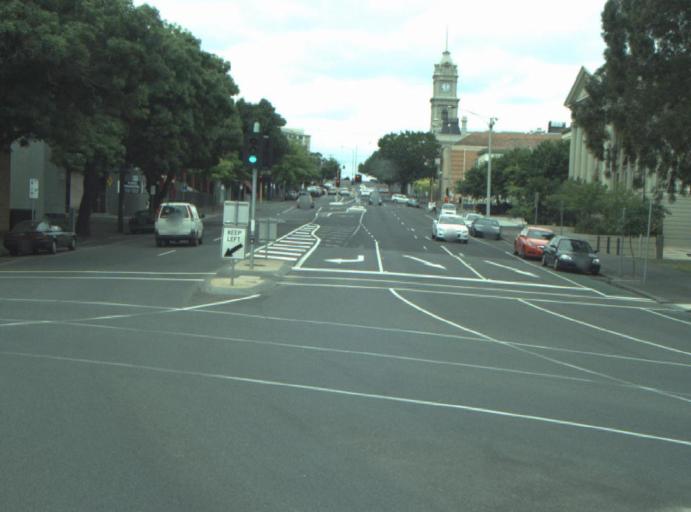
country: AU
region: Victoria
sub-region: Greater Geelong
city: Geelong
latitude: -38.1464
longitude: 144.3583
